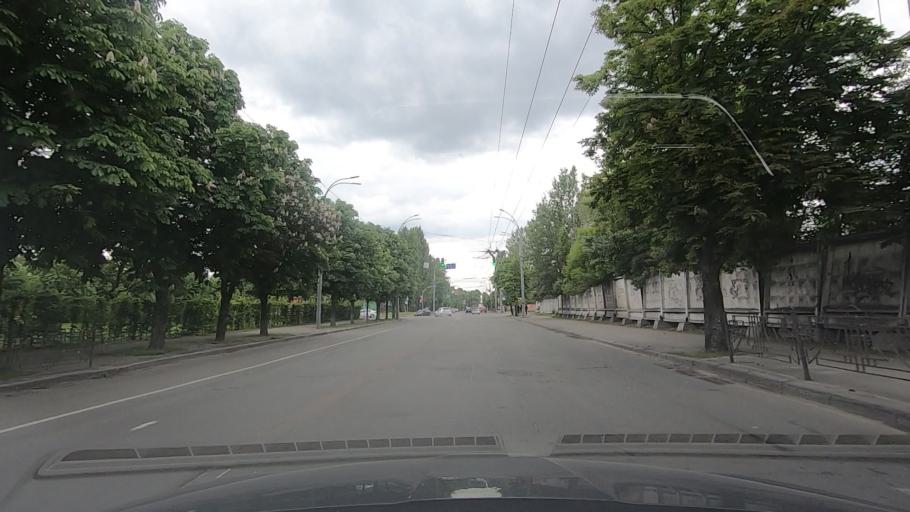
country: MD
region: Drochia
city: Drochia
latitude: 48.0822
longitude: 27.8580
